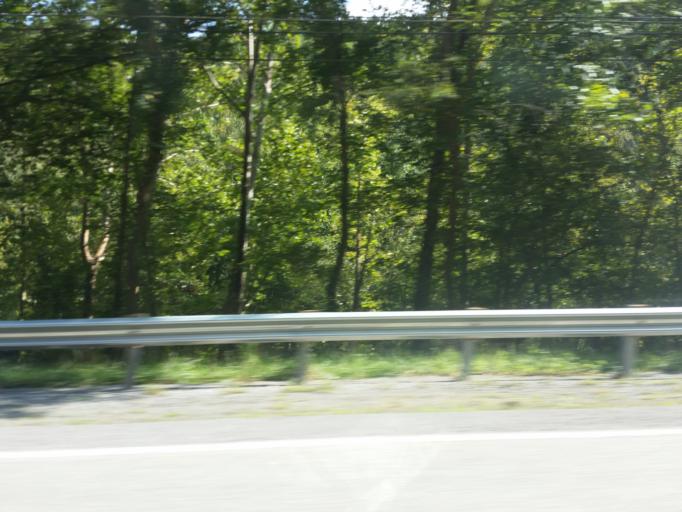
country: US
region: Kentucky
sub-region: Bell County
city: Pineville
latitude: 36.7346
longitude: -83.6092
